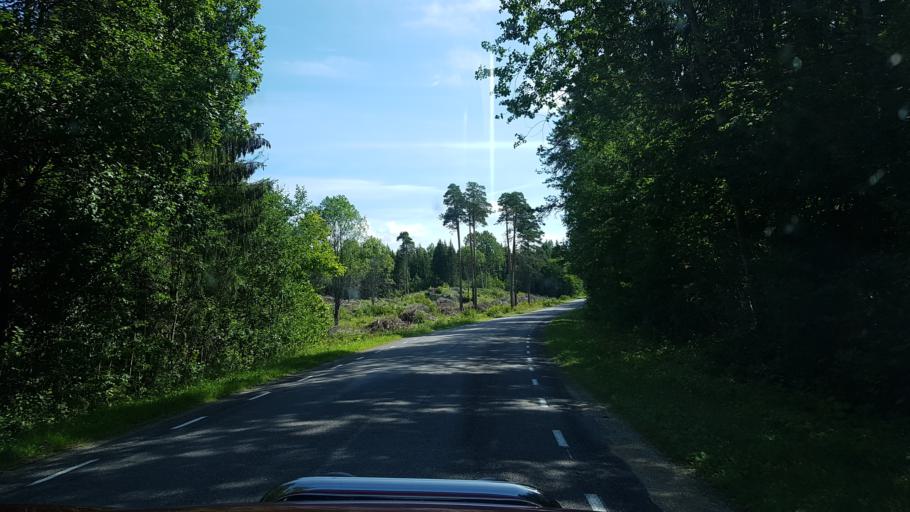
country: EE
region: Laeaene-Virumaa
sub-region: Tapa vald
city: Tapa
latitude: 59.1799
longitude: 25.9778
